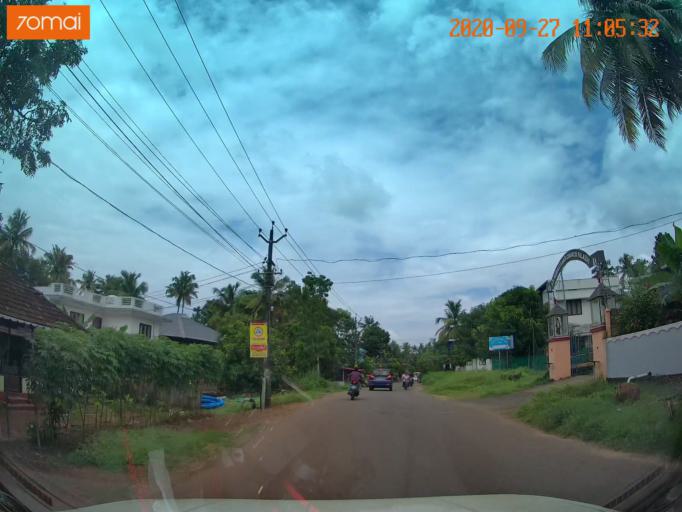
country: IN
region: Kerala
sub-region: Thrissur District
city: Irinjalakuda
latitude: 10.4240
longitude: 76.2468
